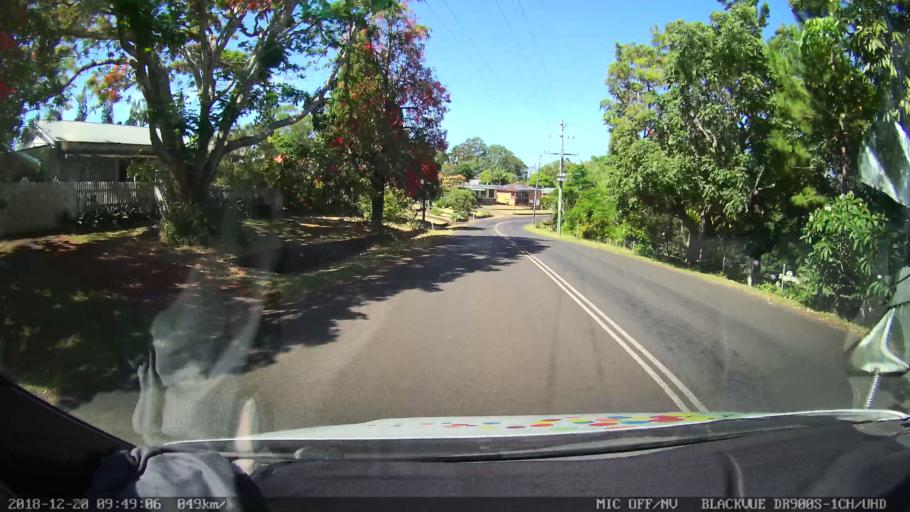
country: AU
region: New South Wales
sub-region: Lismore Municipality
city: Lismore
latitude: -28.7733
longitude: 153.2883
